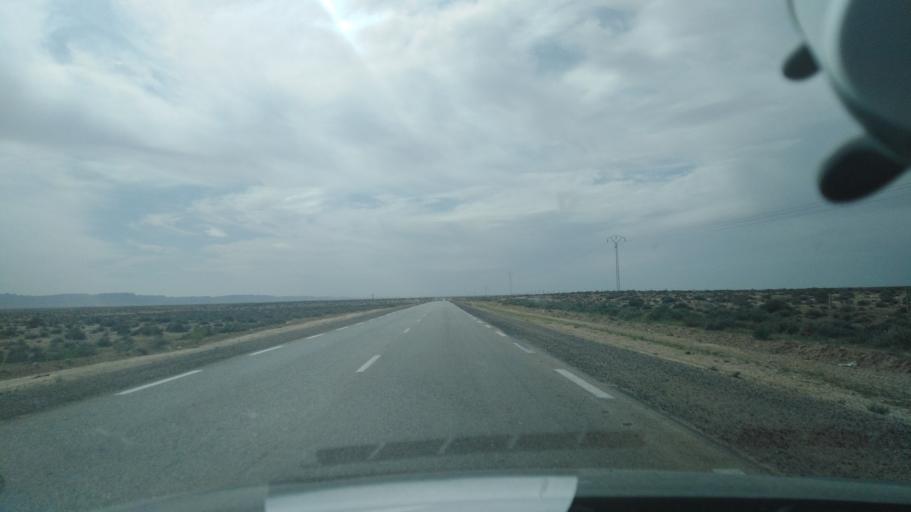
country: TN
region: Qabis
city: Bou Attouche
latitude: 33.8287
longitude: 9.5720
